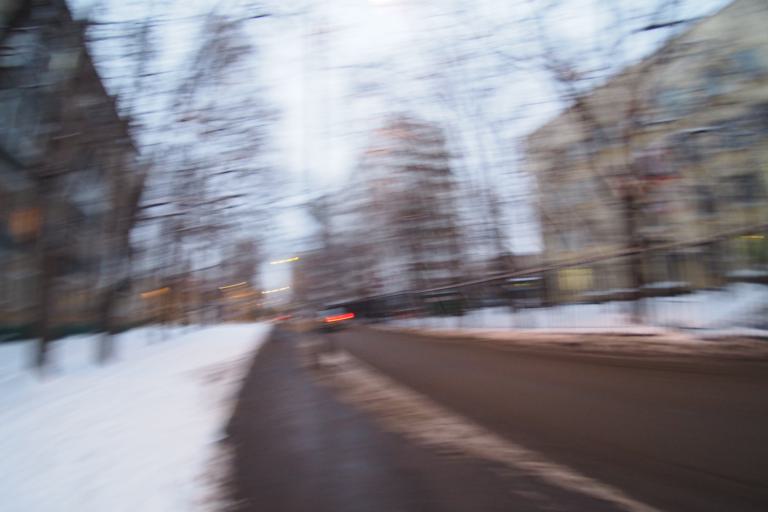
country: RU
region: Moscow
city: Sokol
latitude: 55.8008
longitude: 37.5604
